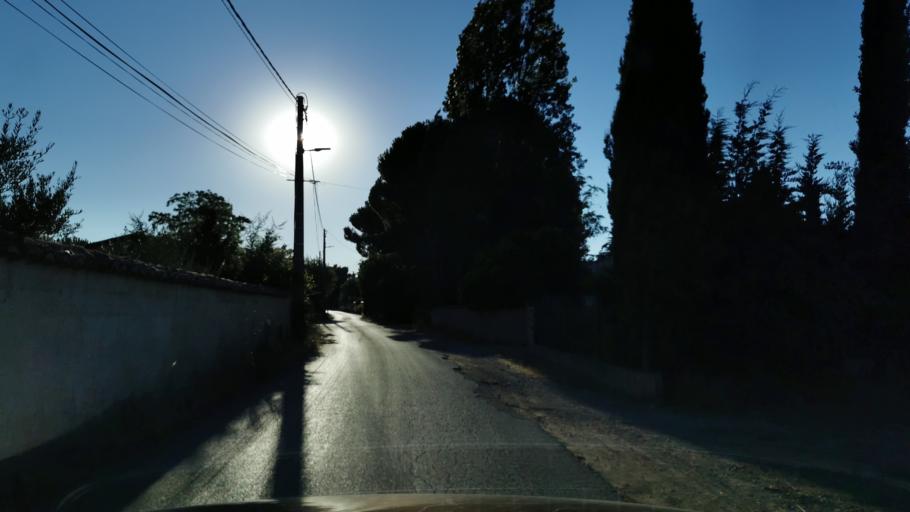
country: FR
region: Languedoc-Roussillon
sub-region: Departement de l'Aude
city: Ouveillan
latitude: 43.2679
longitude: 3.0158
